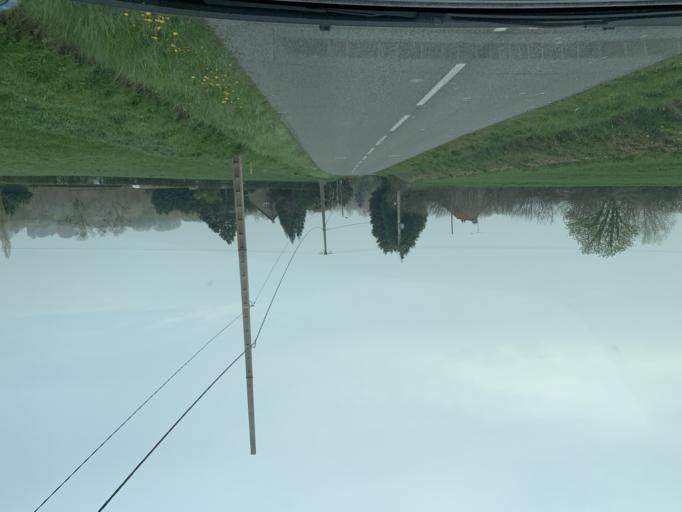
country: FR
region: Nord-Pas-de-Calais
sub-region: Departement du Pas-de-Calais
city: Samer
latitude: 50.6479
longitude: 1.7520
